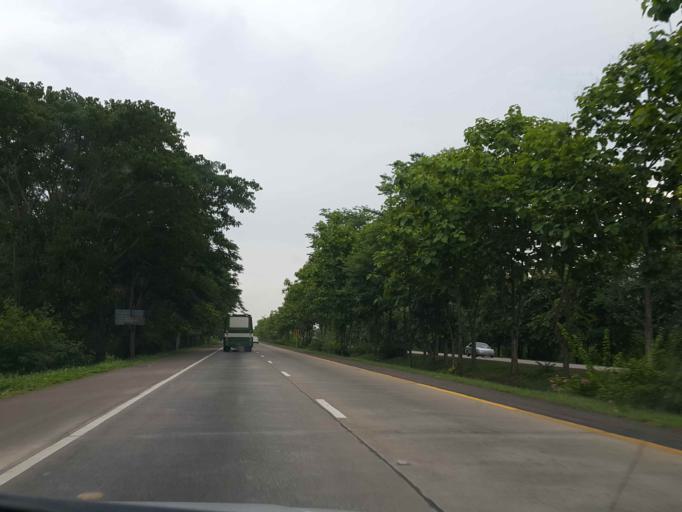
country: TH
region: Lampang
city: Hang Chat
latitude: 18.3204
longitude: 99.3057
